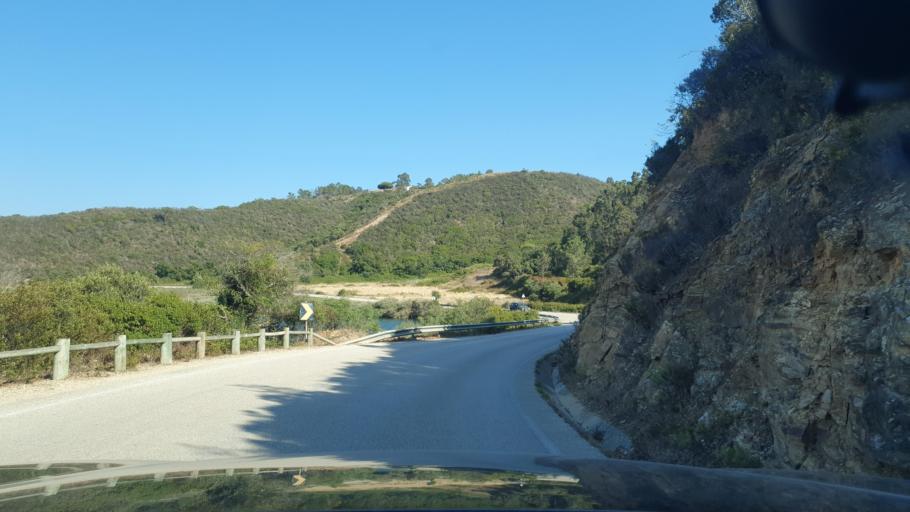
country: PT
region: Beja
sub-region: Odemira
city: Sao Teotonio
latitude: 37.4348
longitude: -8.7896
